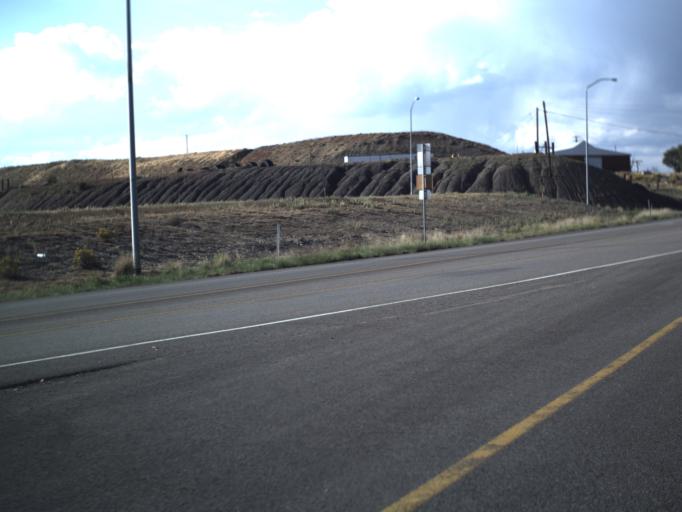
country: US
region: Utah
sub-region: Carbon County
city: Price
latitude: 39.5877
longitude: -110.7888
